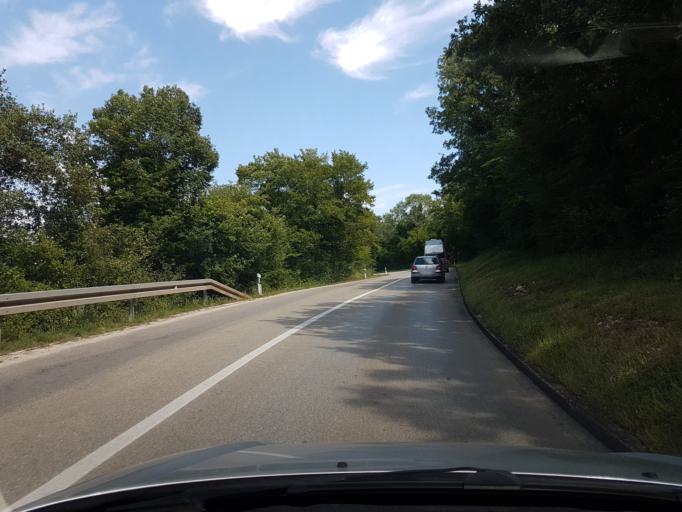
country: HR
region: Istarska
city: Vrsar
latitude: 45.1532
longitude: 13.6420
